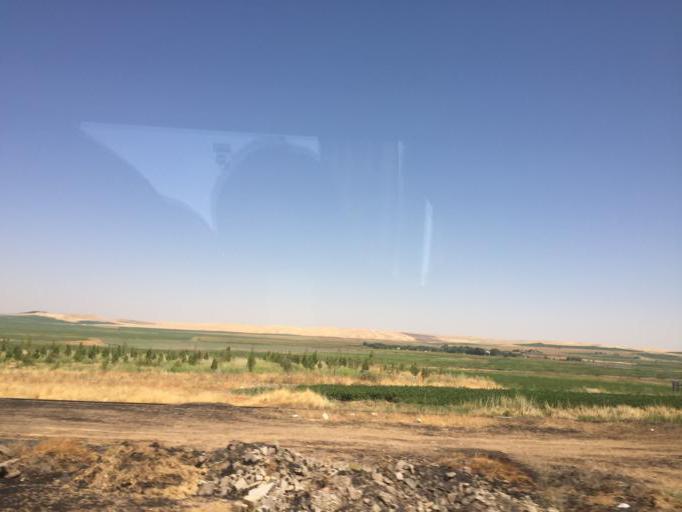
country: TR
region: Diyarbakir
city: Tepe
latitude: 37.8488
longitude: 40.7950
